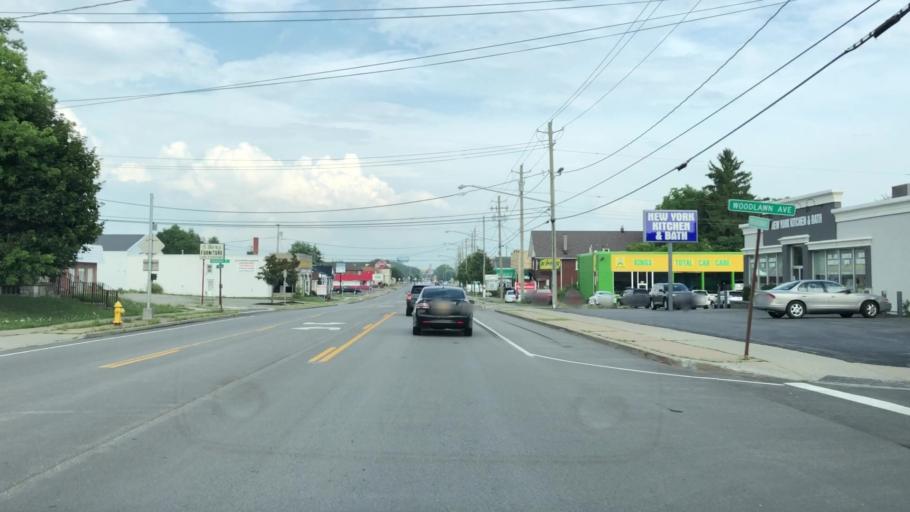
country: US
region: New York
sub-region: Erie County
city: Depew
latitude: 42.9017
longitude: -78.6921
